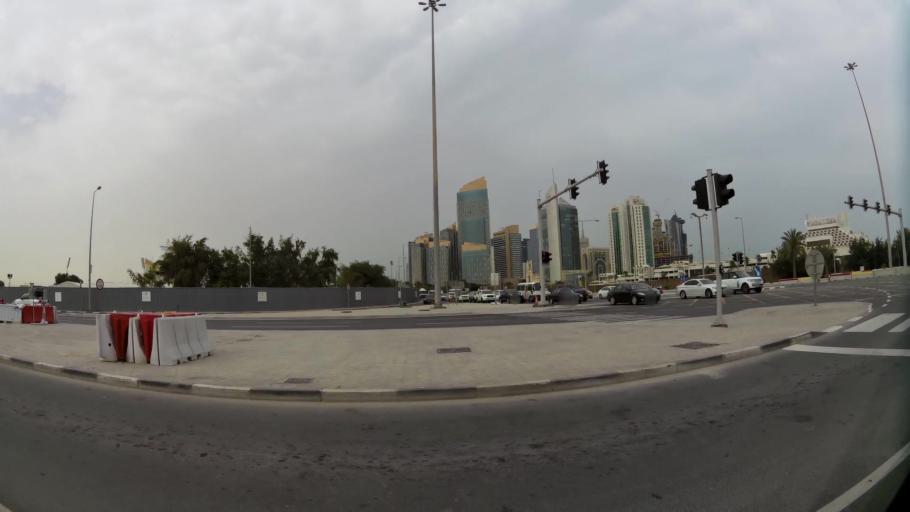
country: QA
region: Baladiyat ad Dawhah
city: Doha
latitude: 25.3097
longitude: 51.5146
